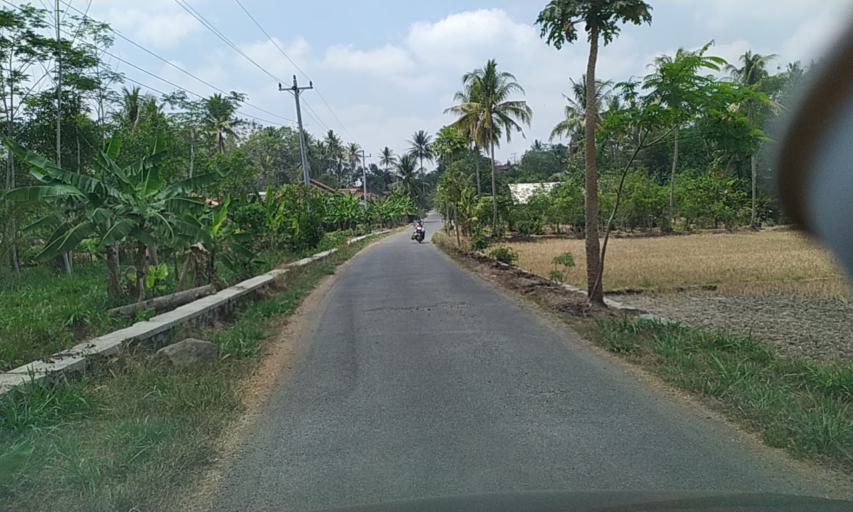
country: ID
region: Central Java
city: Prapagan
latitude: -7.5807
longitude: 108.9440
